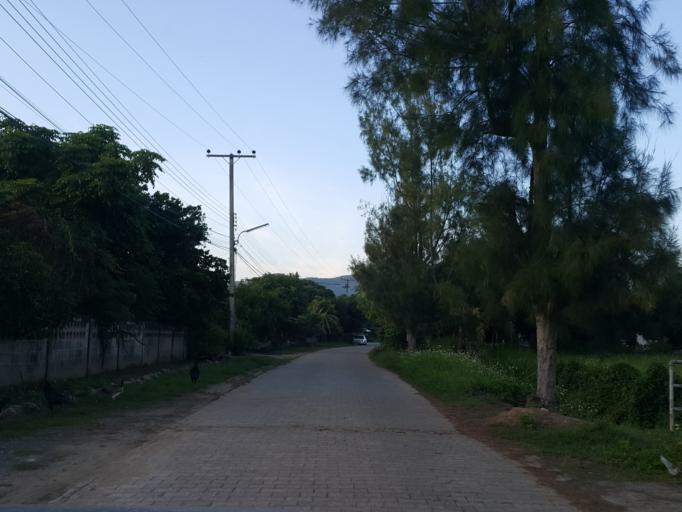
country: TH
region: Chiang Mai
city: Mae On
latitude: 18.7174
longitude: 99.2016
